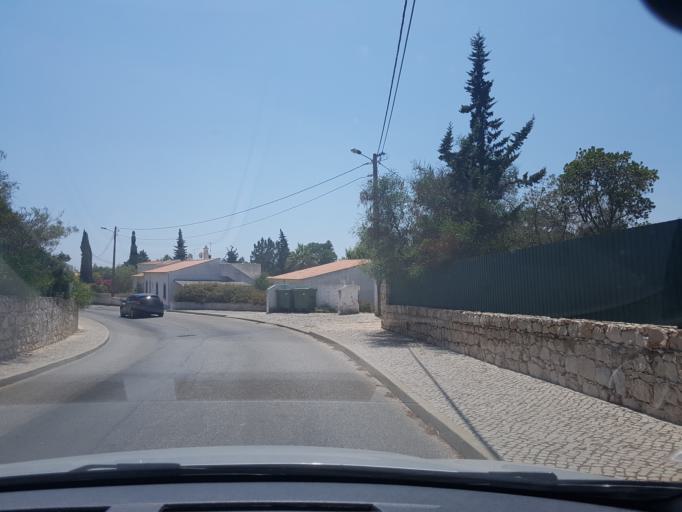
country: PT
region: Faro
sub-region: Lagoa
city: Carvoeiro
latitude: 37.0983
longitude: -8.4587
